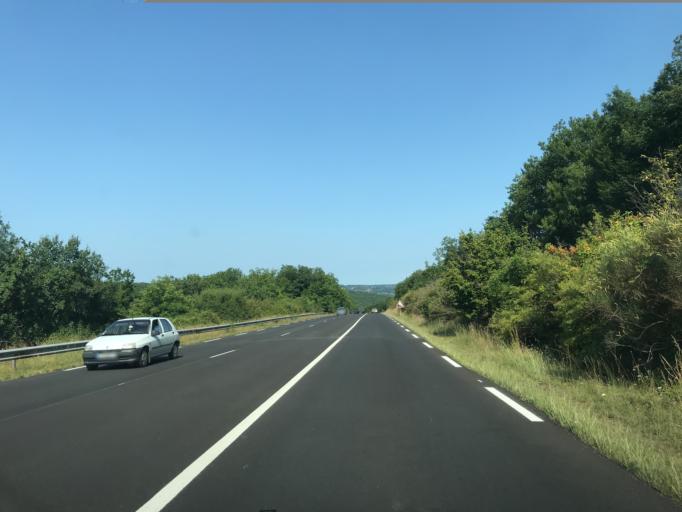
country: FR
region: Aquitaine
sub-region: Departement de la Dordogne
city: Montignac
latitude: 45.0467
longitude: 1.2228
